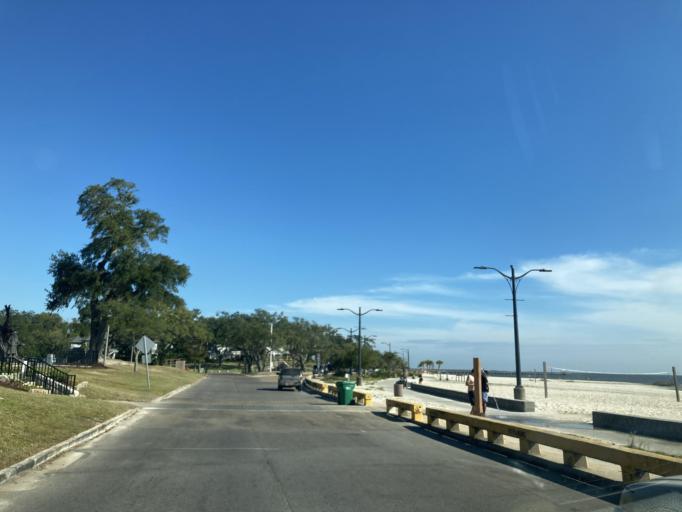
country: US
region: Mississippi
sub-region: Jackson County
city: Ocean Springs
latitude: 30.4056
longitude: -88.8294
